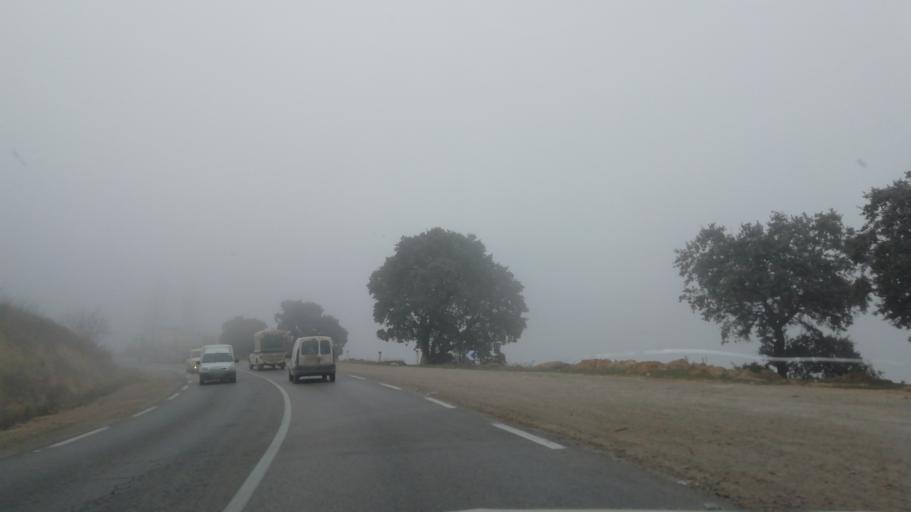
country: DZ
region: Mascara
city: Mascara
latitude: 35.5278
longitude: 0.3331
